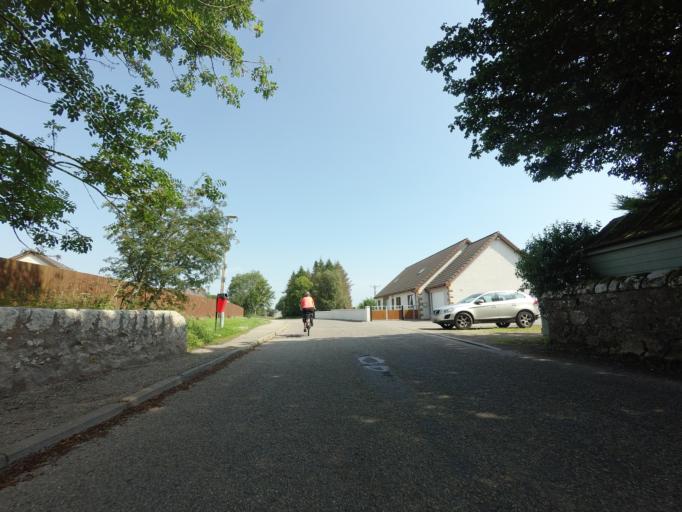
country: GB
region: Scotland
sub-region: Highland
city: Tain
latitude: 57.8040
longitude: -4.0645
